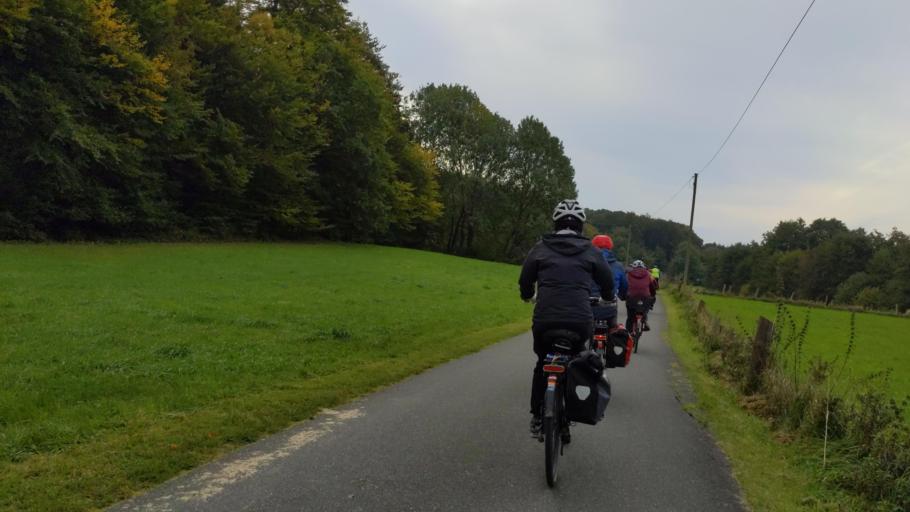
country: DE
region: Schleswig-Holstein
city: Rehhorst
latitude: 53.8626
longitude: 10.4740
